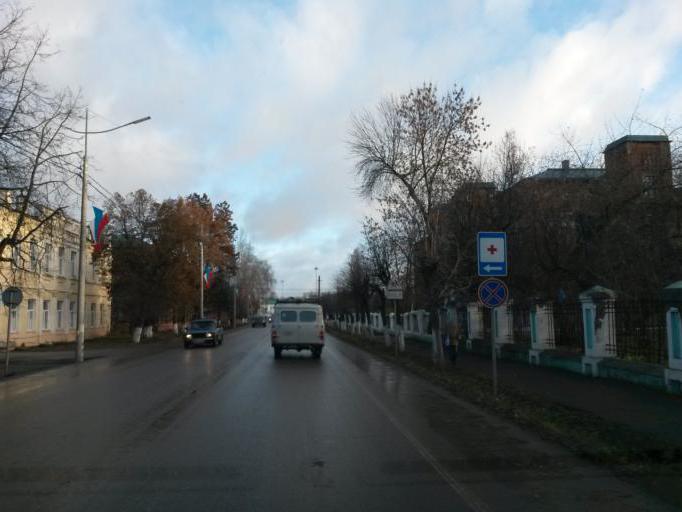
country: RU
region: Jaroslavl
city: Pereslavl'-Zalesskiy
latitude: 56.7363
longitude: 38.8539
